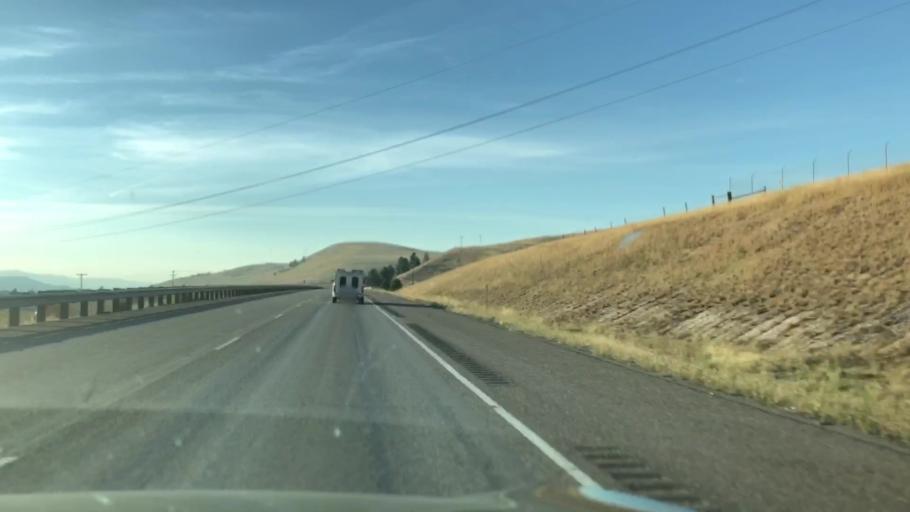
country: US
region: Montana
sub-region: Missoula County
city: Missoula
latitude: 46.9081
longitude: -114.0252
